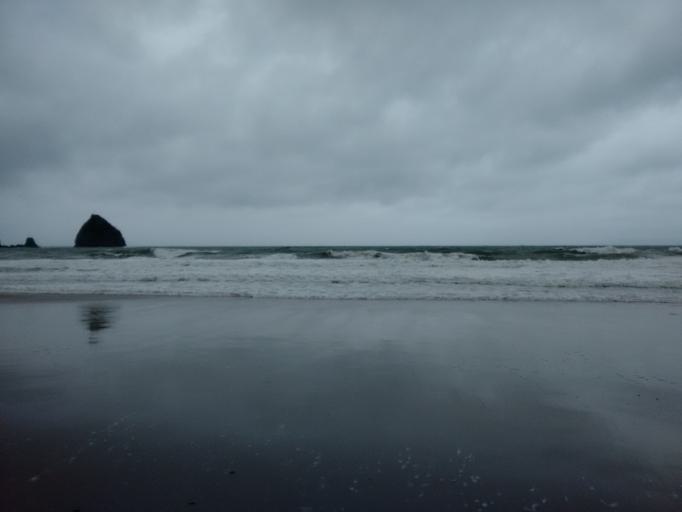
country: NZ
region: Waikato
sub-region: Thames-Coromandel District
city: Coromandel
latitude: -36.6992
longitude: 175.6077
